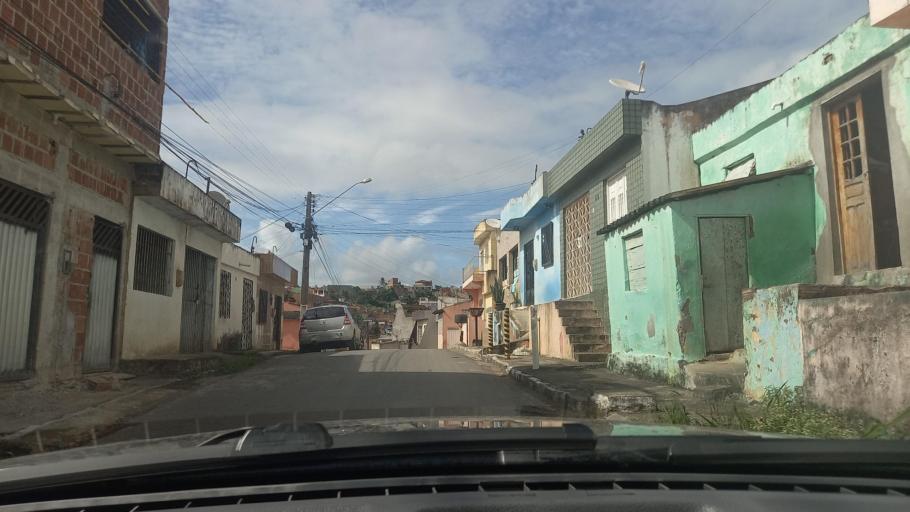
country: BR
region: Pernambuco
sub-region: Vitoria De Santo Antao
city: Vitoria de Santo Antao
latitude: -8.1244
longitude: -35.2869
